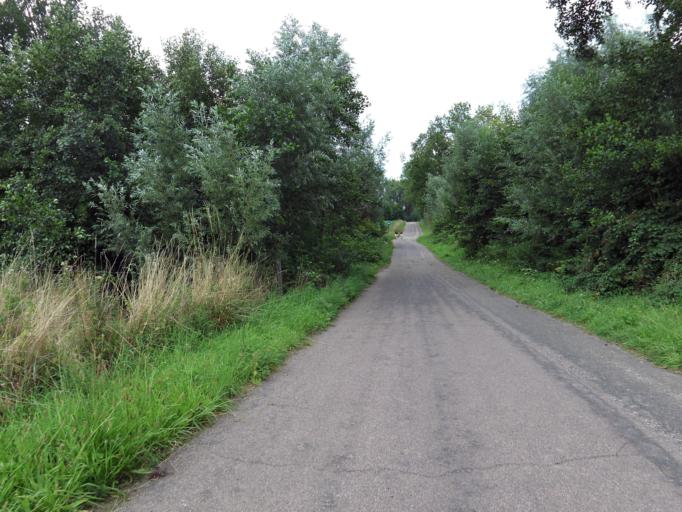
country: NL
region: Limburg
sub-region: Gemeente Kerkrade
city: Kerkrade
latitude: 50.8812
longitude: 6.0476
